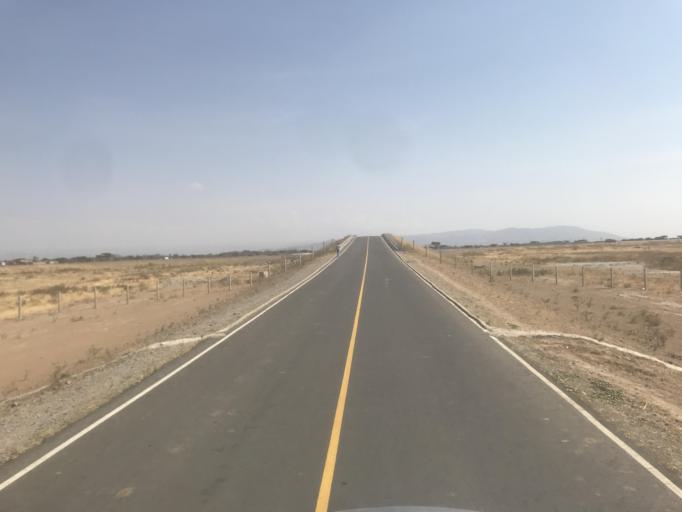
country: ET
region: Oromiya
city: Ziway
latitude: 7.9603
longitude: 38.6925
